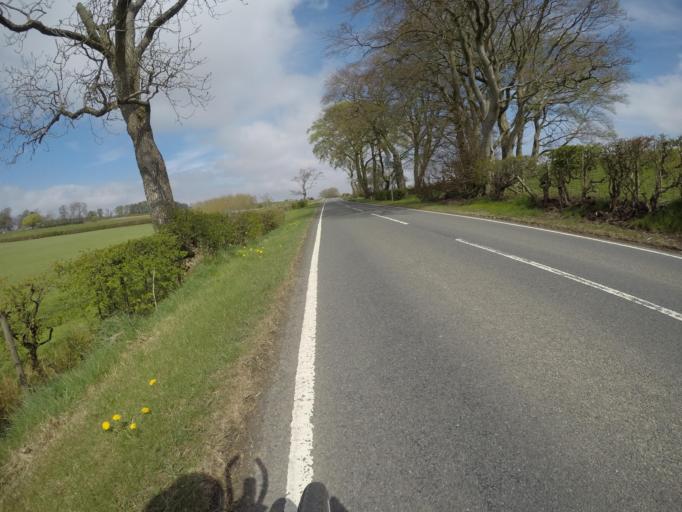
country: GB
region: Scotland
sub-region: East Ayrshire
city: Stewarton
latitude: 55.7074
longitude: -4.4607
